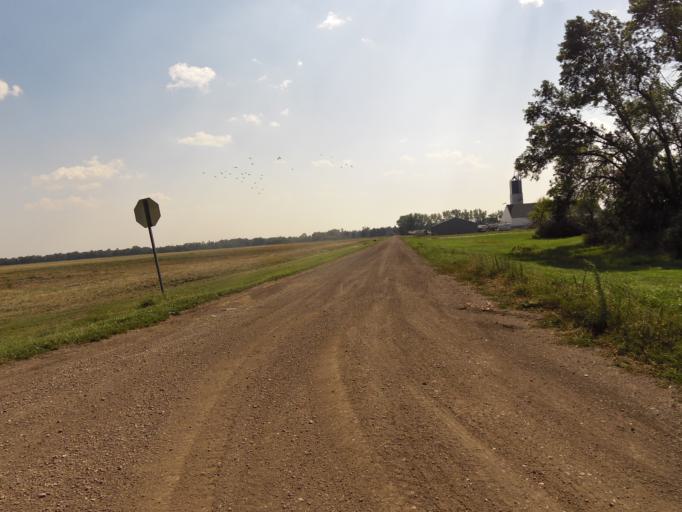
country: US
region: North Dakota
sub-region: Walsh County
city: Grafton
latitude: 48.4341
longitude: -97.3971
